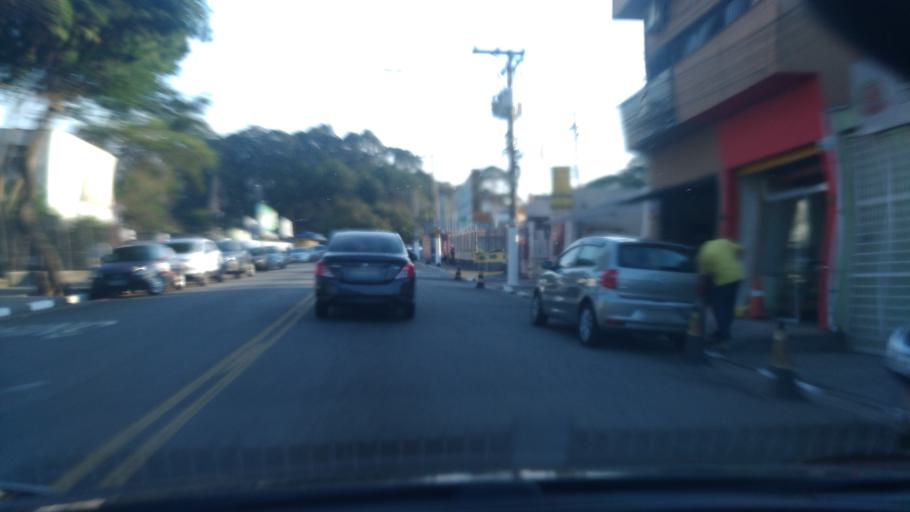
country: BR
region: Sao Paulo
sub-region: Osasco
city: Osasco
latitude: -23.5351
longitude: -46.7919
